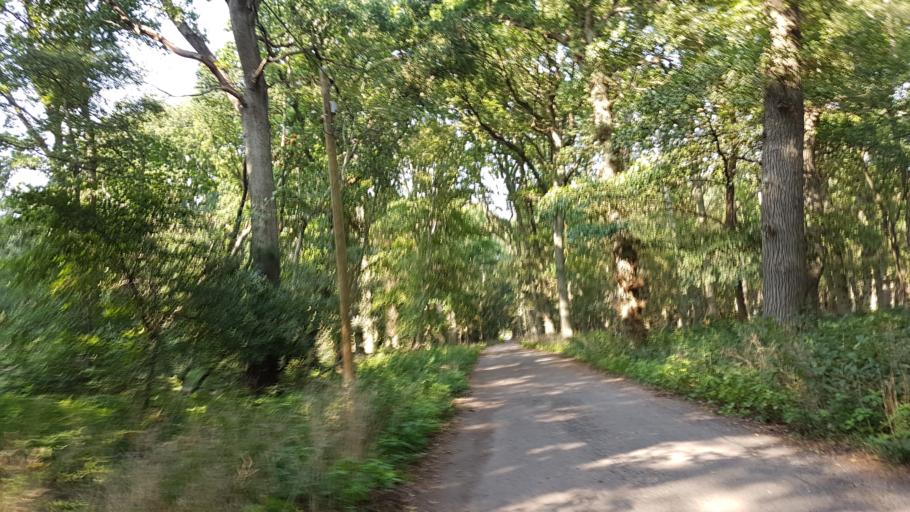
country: DE
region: Mecklenburg-Vorpommern
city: Glowe
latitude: 54.5615
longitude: 13.4611
